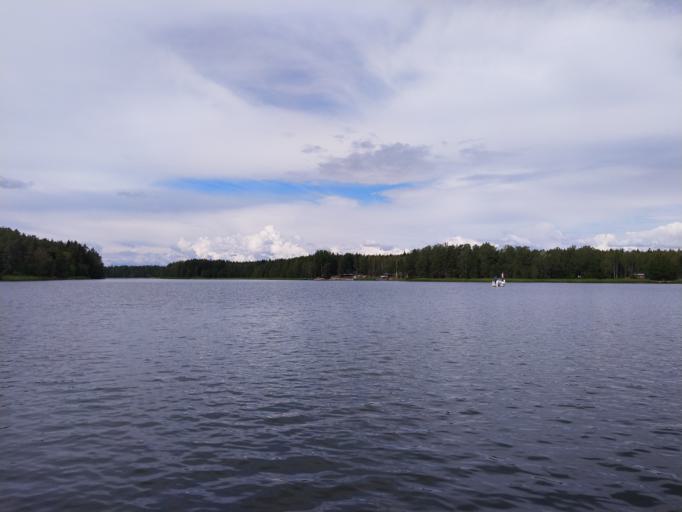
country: FI
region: Uusimaa
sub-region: Raaseporin
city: Karis
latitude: 59.9689
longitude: 23.7031
